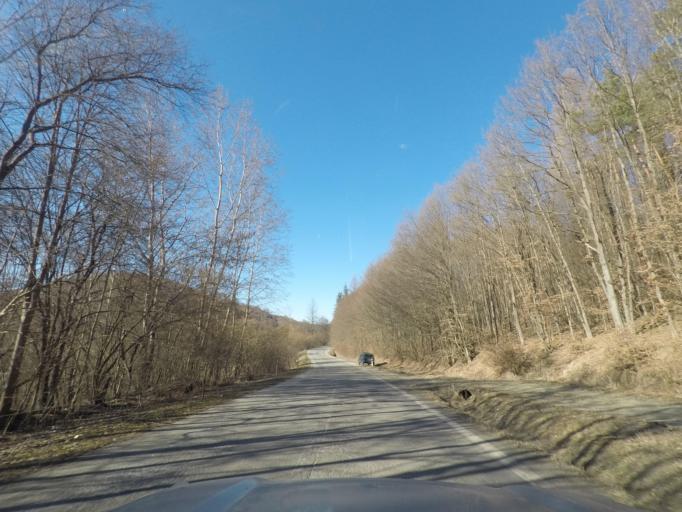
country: SK
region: Presovsky
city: Snina
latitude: 49.0385
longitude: 22.1741
